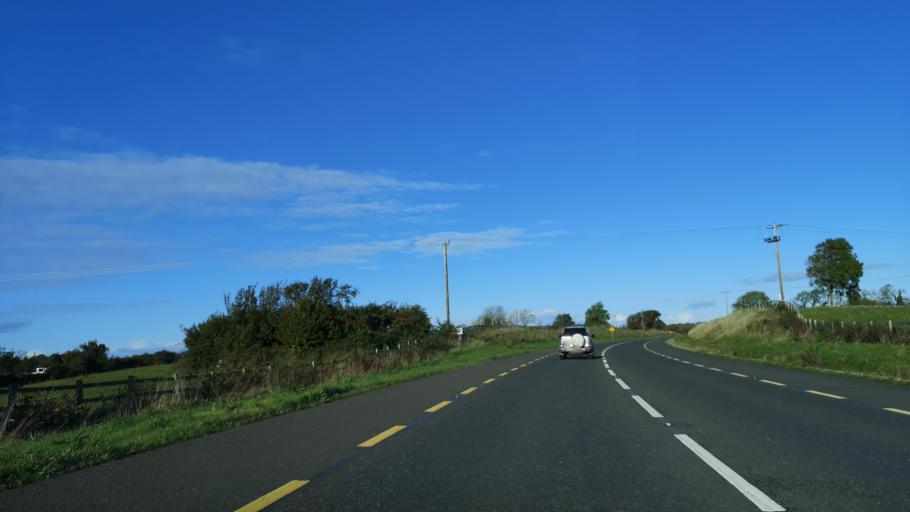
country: IE
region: Connaught
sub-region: County Galway
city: Claregalway
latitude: 53.4287
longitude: -9.0533
